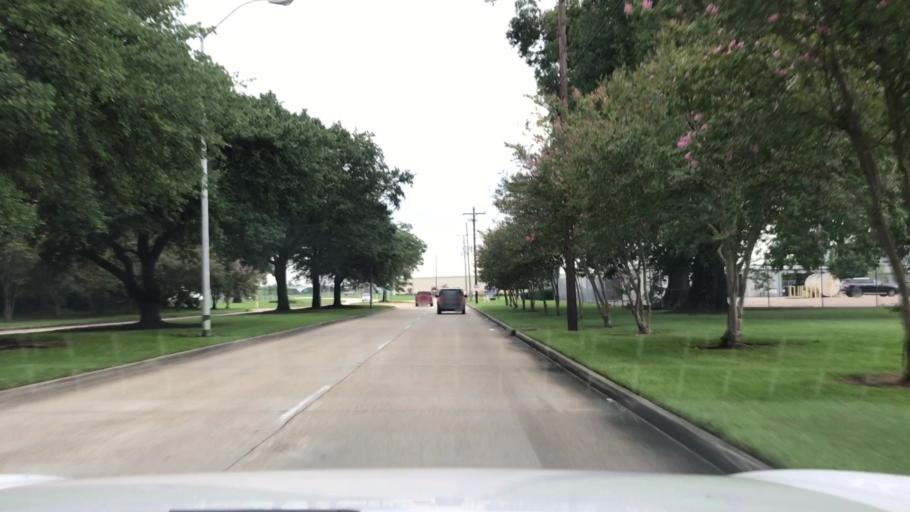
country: US
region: Louisiana
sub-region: East Baton Rouge Parish
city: Brownsfield
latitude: 30.5346
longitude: -91.1612
